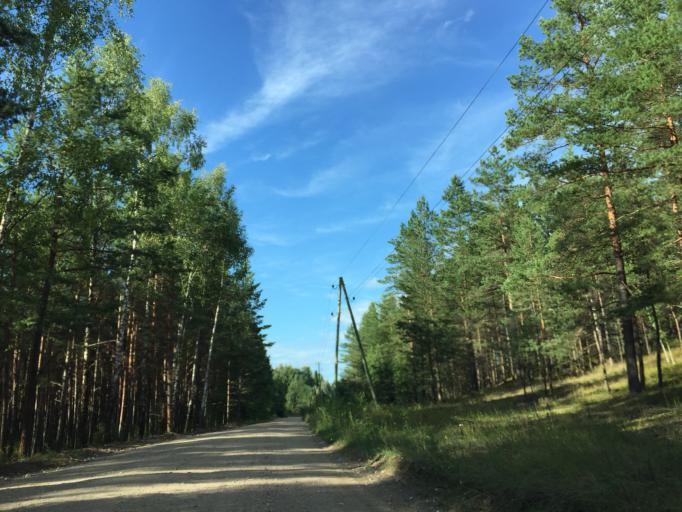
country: LV
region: Saulkrastu
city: Saulkrasti
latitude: 57.1881
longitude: 24.3637
